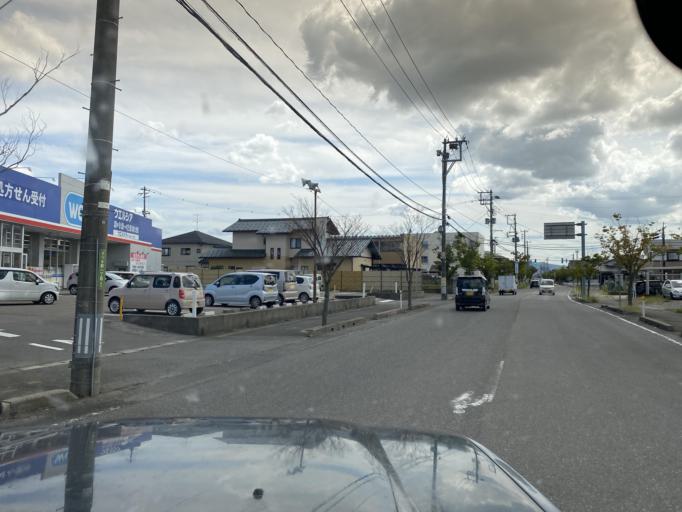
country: JP
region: Niigata
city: Niitsu-honcho
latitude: 37.8141
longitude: 139.1161
